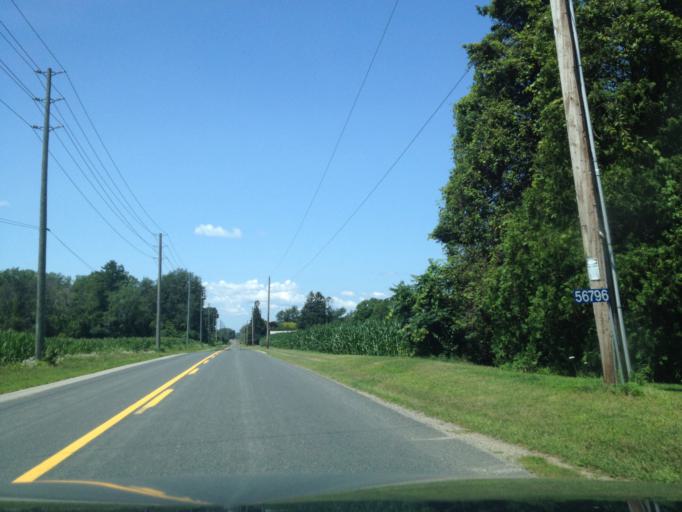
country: CA
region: Ontario
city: Aylmer
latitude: 42.6459
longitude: -80.7500
